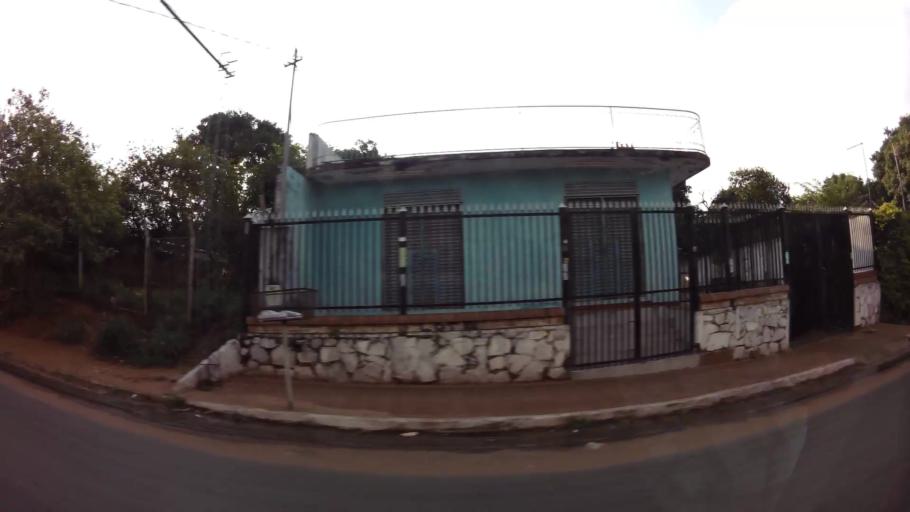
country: PY
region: Central
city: Nemby
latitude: -25.3674
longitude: -57.5309
